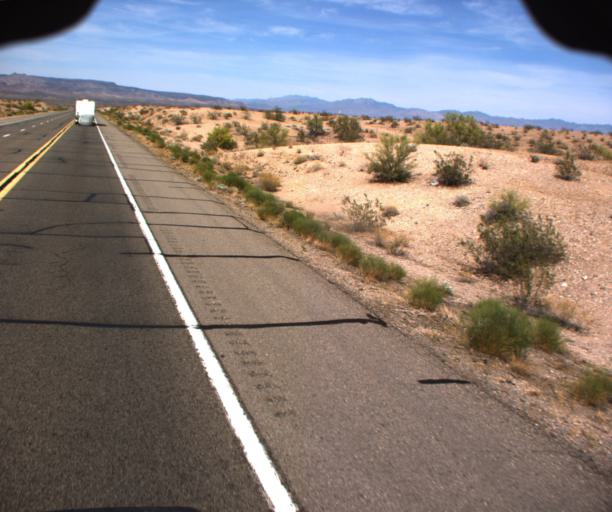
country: US
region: Arizona
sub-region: Mohave County
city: Desert Hills
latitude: 34.6814
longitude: -114.3055
